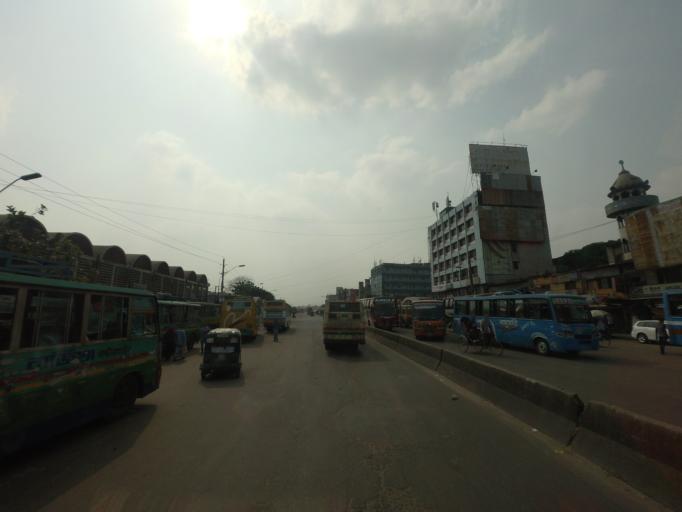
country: BD
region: Dhaka
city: Azimpur
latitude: 23.7833
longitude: 90.3437
